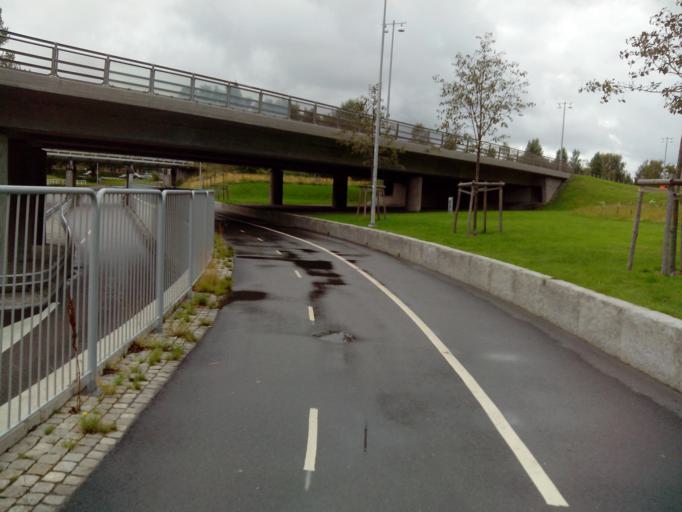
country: SE
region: Vaestra Goetaland
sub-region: Goteborg
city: Goeteborg
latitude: 57.7135
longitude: 11.9434
